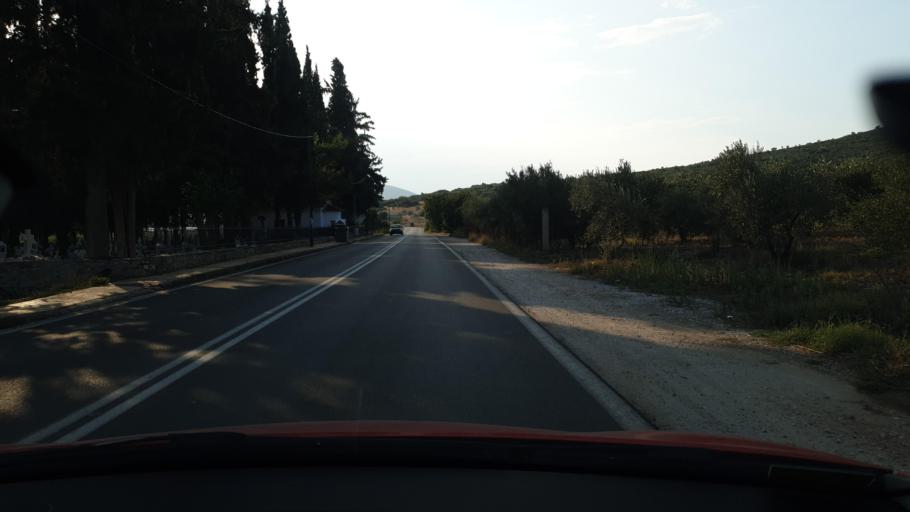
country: GR
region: Thessaly
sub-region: Nomos Magnisias
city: Sourpi
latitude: 39.1084
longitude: 22.8898
